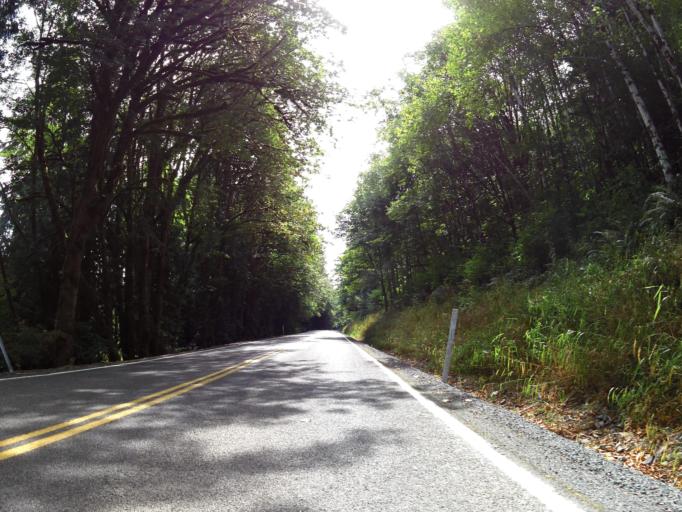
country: US
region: Washington
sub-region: Lewis County
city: Napavine
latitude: 46.5554
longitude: -122.9585
